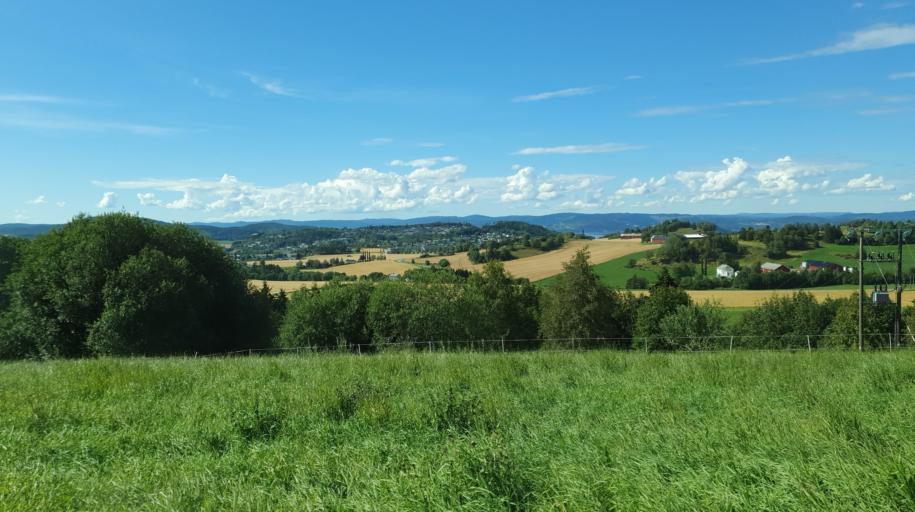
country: NO
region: Nord-Trondelag
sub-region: Levanger
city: Skogn
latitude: 63.6937
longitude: 11.2335
